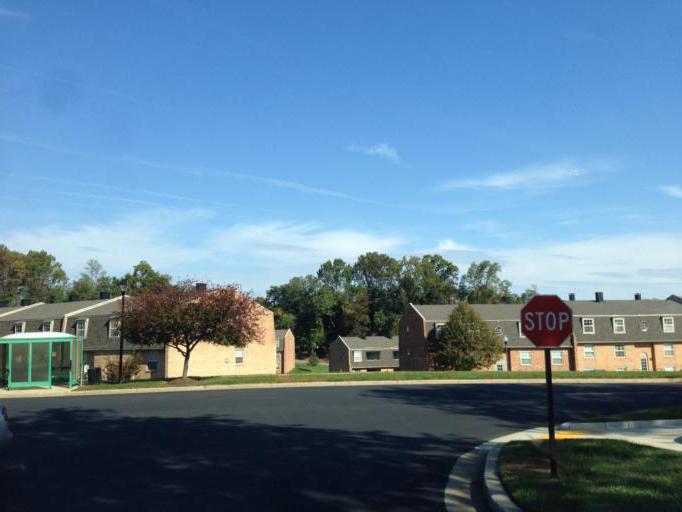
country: US
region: Maryland
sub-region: Howard County
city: Ellicott City
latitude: 39.2868
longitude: -76.8162
